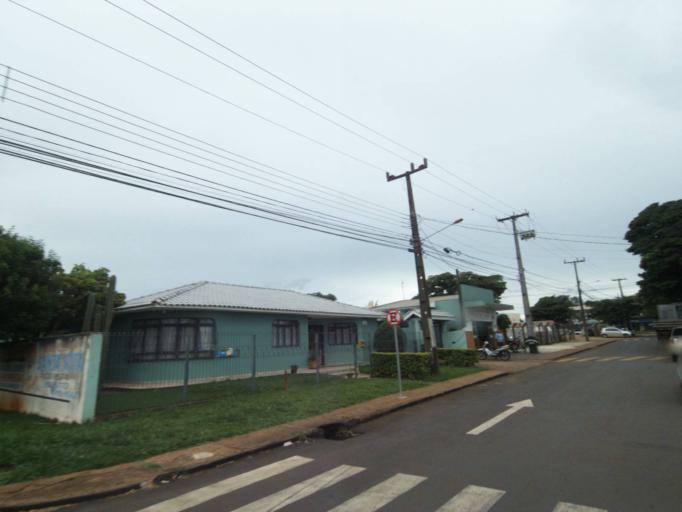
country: BR
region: Parana
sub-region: Campo Mourao
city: Campo Mourao
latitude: -24.0254
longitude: -52.3632
